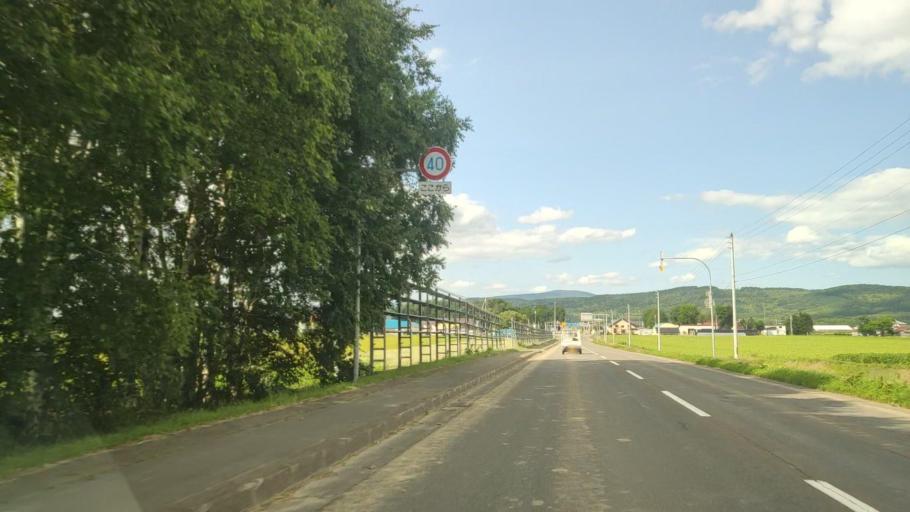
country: JP
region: Hokkaido
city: Nayoro
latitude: 44.4333
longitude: 142.4019
